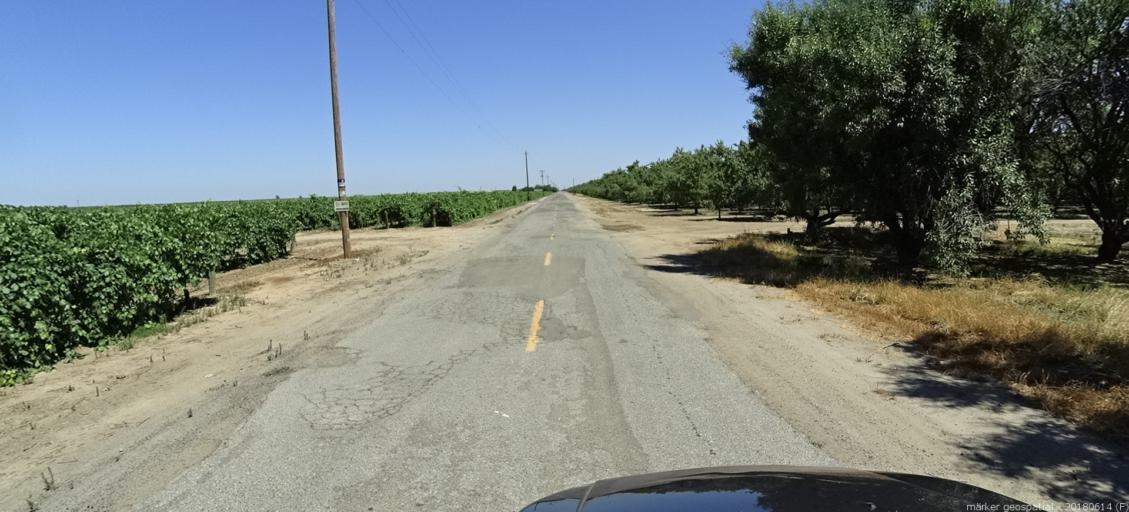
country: US
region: California
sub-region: Madera County
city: Fairmead
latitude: 37.0217
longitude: -120.2387
